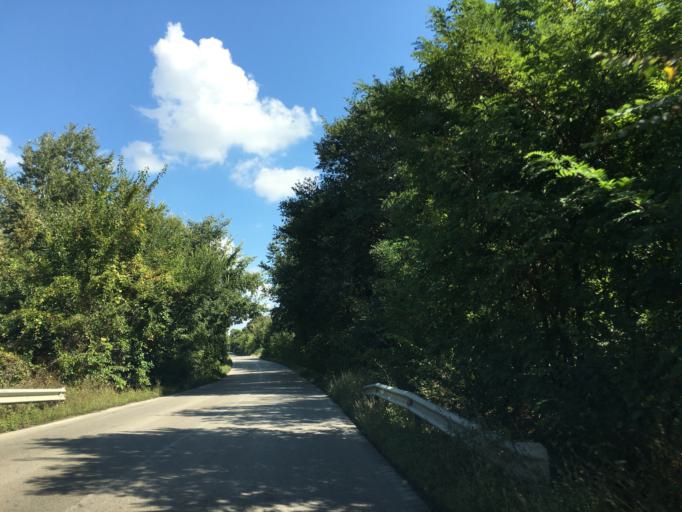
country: BG
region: Montana
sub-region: Obshtina Lom
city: Lom
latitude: 43.7961
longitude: 23.1319
